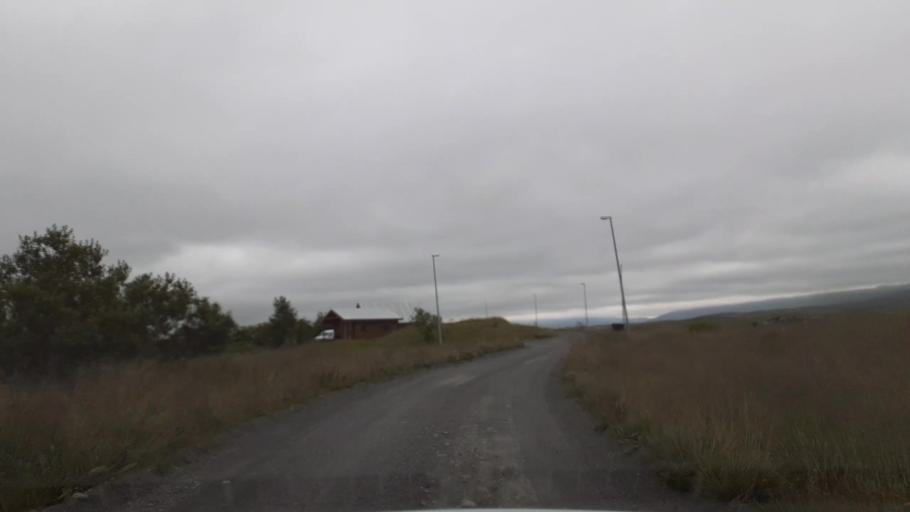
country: IS
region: Northwest
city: Saudarkrokur
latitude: 65.5499
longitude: -19.4557
